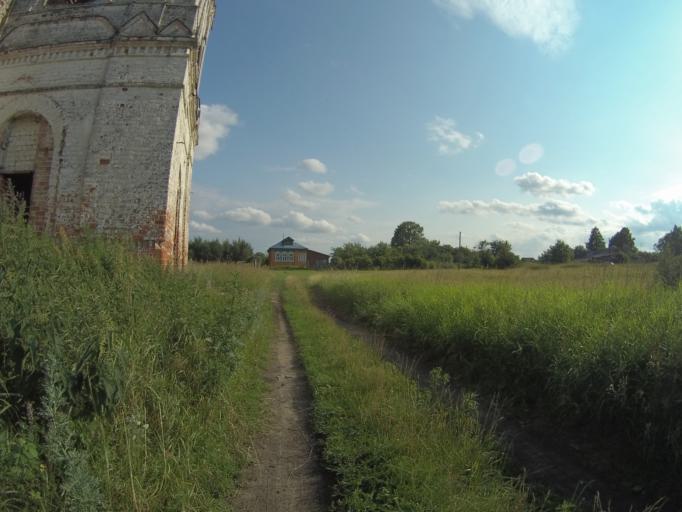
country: RU
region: Vladimir
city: Orgtrud
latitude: 56.3423
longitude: 40.6913
